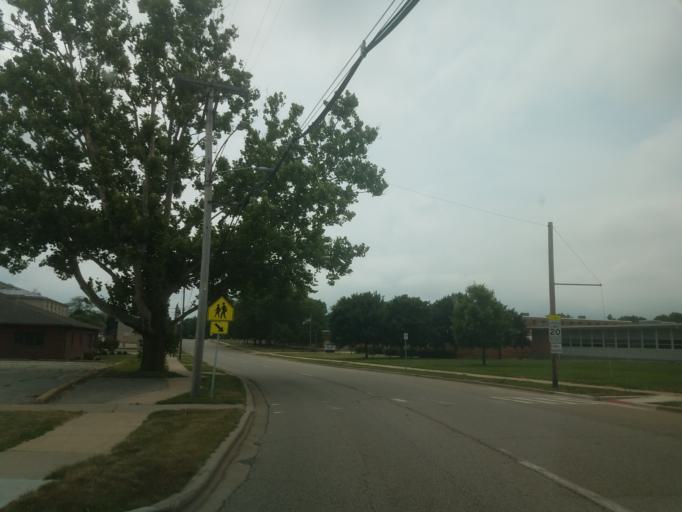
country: US
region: Illinois
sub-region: McLean County
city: Normal
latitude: 40.5089
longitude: -88.9965
